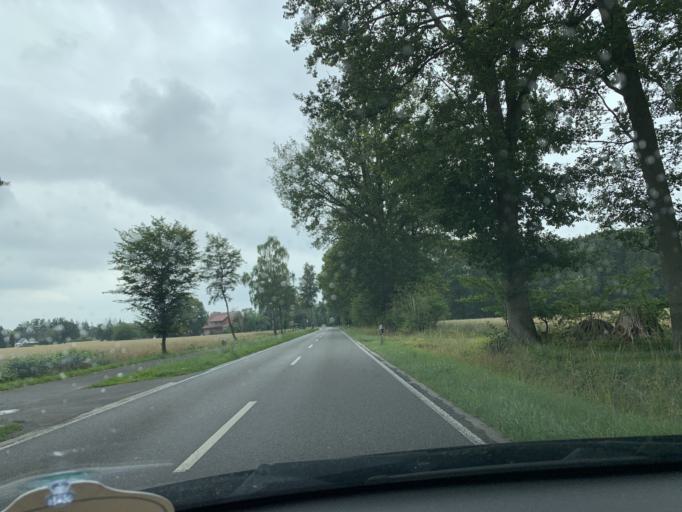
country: DE
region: North Rhine-Westphalia
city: Lengerich
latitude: 52.1590
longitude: 7.8455
